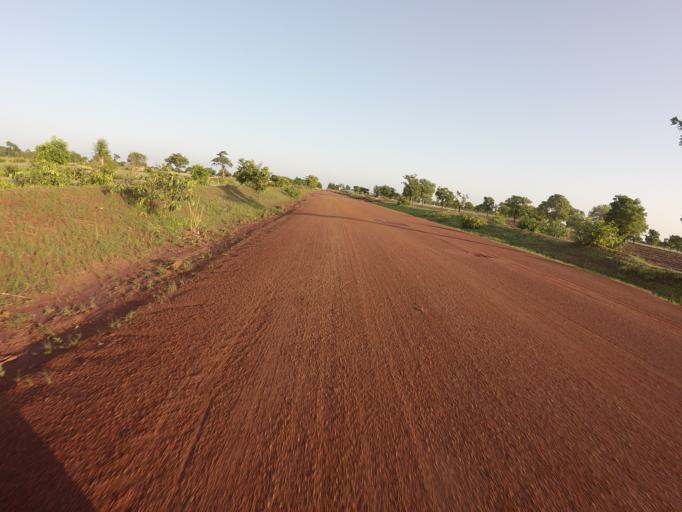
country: TG
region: Savanes
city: Sansanne-Mango
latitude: 10.2697
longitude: -0.0815
